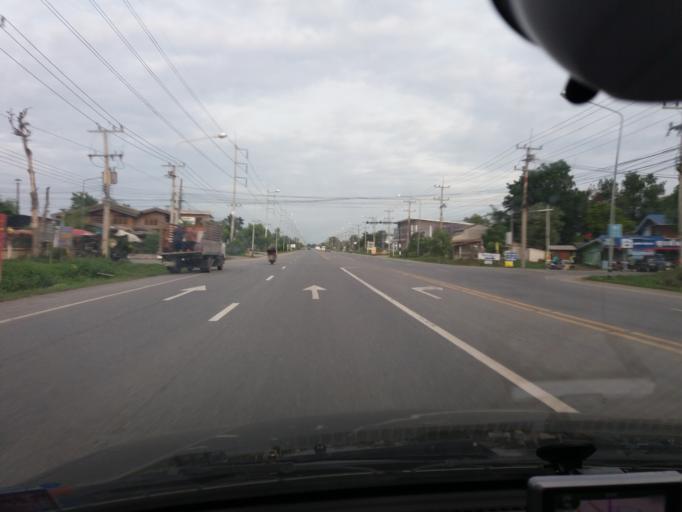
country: TH
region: Suphan Buri
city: U Thong
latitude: 14.3348
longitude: 99.7835
